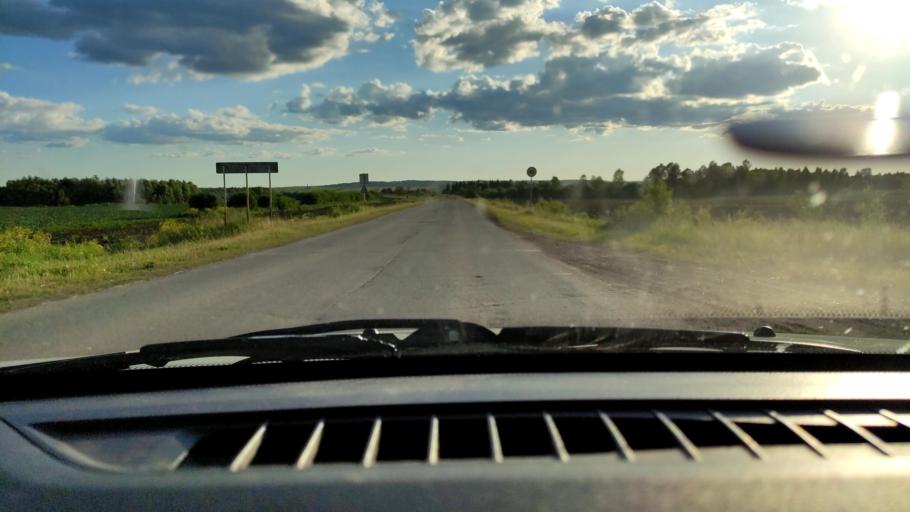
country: RU
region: Perm
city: Uinskoye
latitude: 57.0764
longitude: 56.6048
